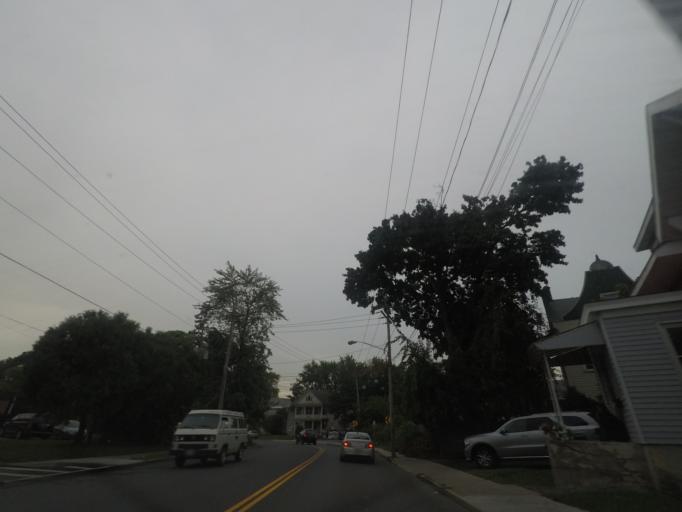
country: US
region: New York
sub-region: Albany County
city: Albany
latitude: 42.6405
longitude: -73.7853
